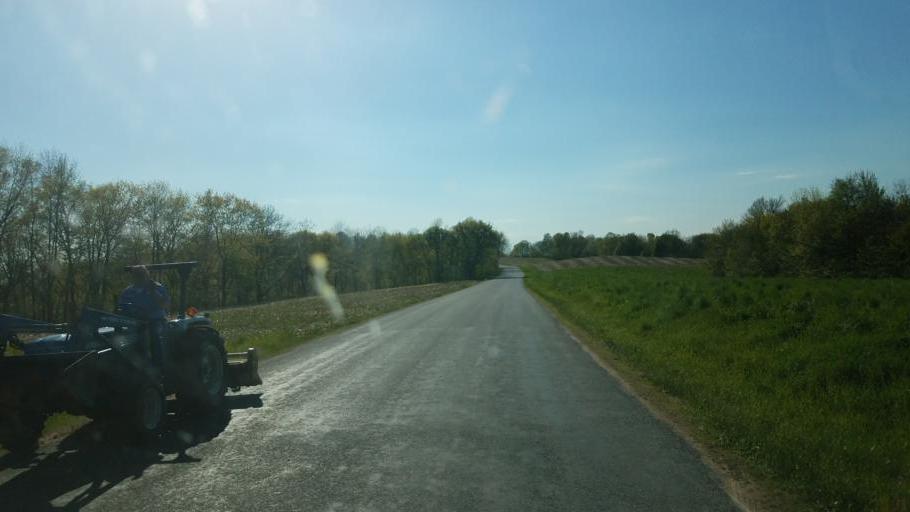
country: US
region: Wisconsin
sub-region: Vernon County
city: Hillsboro
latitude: 43.6743
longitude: -90.3585
